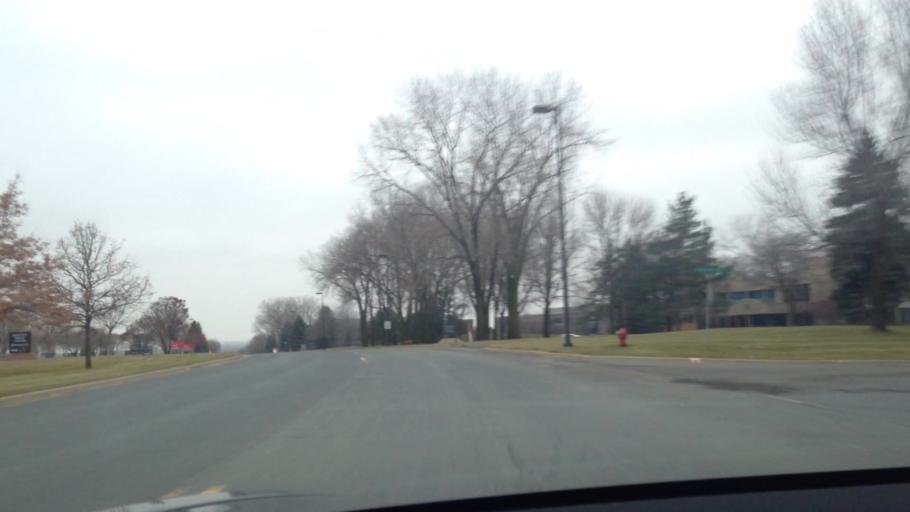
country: US
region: Minnesota
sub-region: Dakota County
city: Mendota Heights
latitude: 44.8636
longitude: -93.1560
